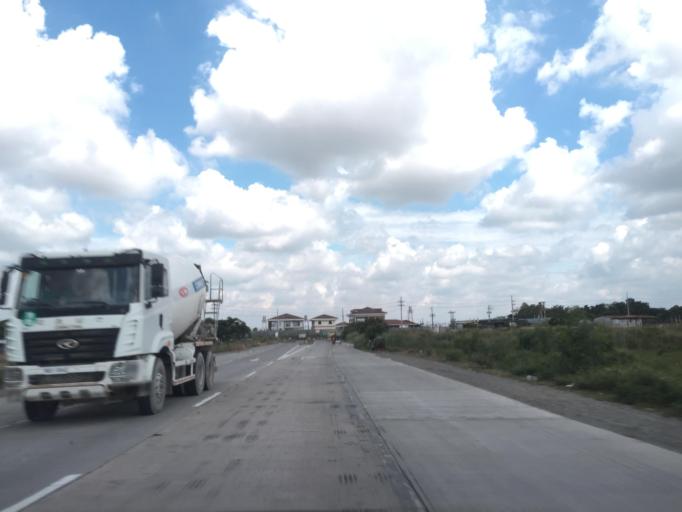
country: PH
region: Central Luzon
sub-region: Province of Tarlac
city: Salcedo
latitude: 15.8703
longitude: 120.6052
